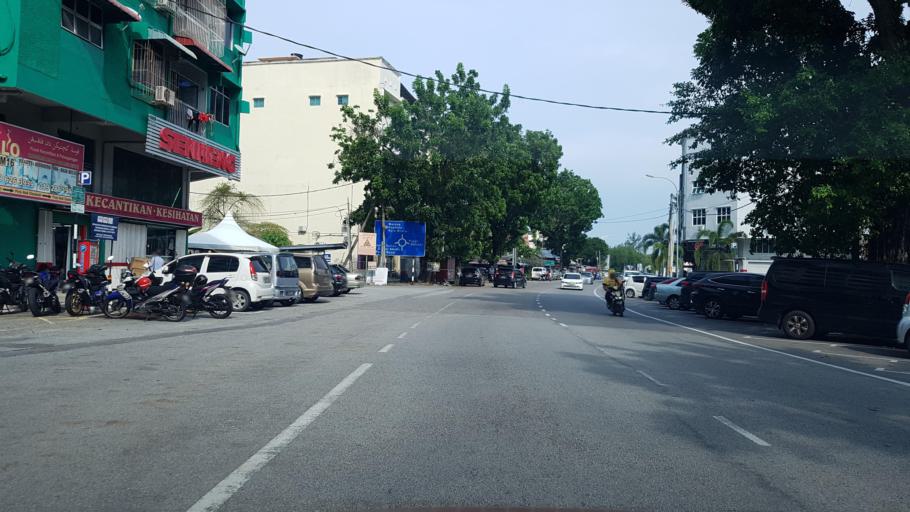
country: MY
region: Terengganu
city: Kuala Terengganu
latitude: 5.3306
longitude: 103.1449
